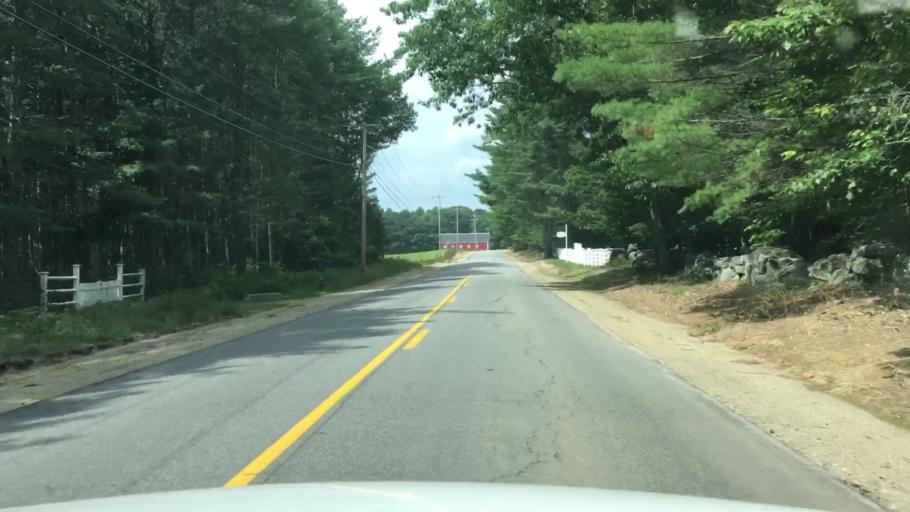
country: US
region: Maine
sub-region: Oxford County
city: Rumford
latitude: 44.5326
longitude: -70.6670
